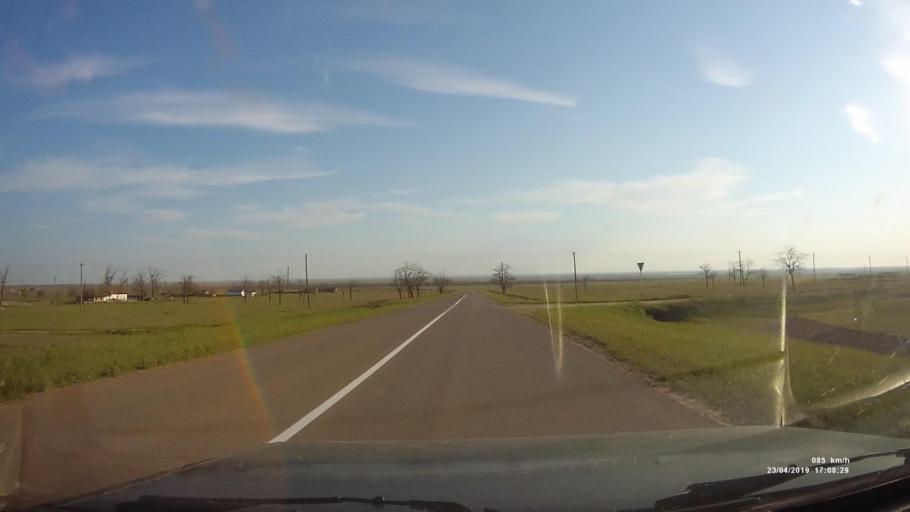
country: RU
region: Kalmykiya
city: Priyutnoye
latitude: 46.2709
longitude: 43.4874
